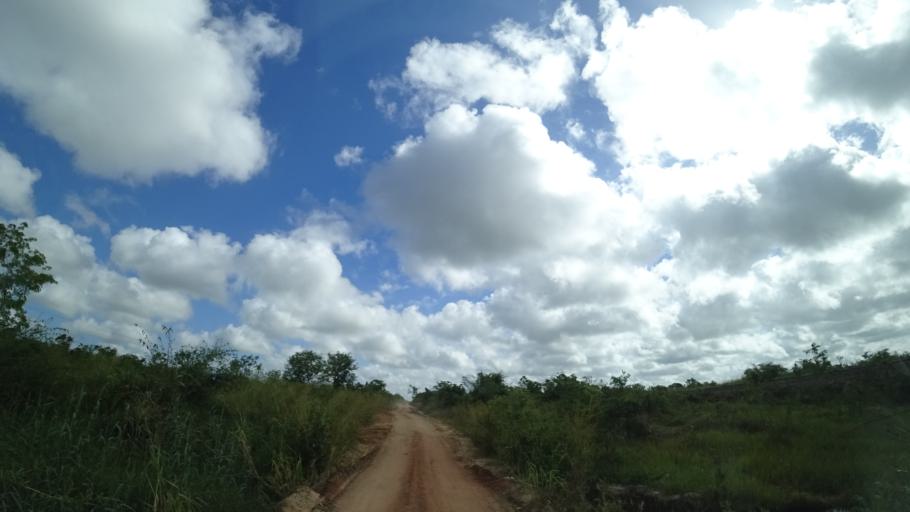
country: MZ
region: Sofala
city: Dondo
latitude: -19.4449
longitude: 34.7164
